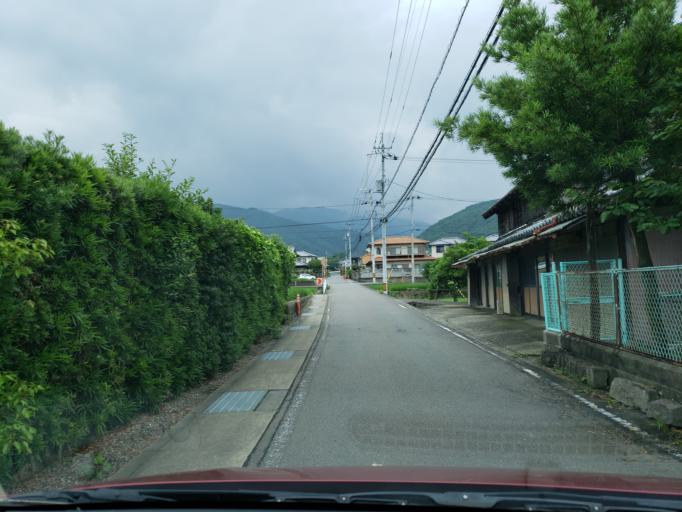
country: JP
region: Tokushima
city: Wakimachi
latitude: 34.0942
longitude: 134.2286
